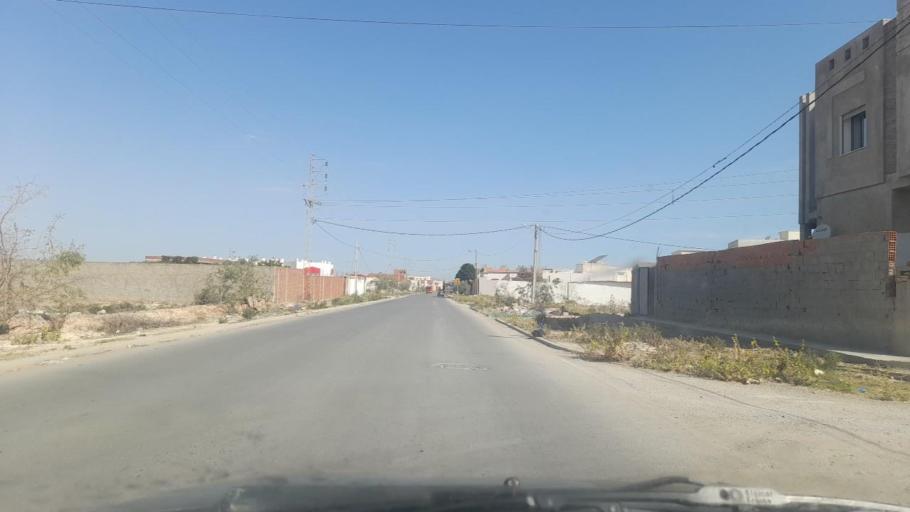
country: TN
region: Susah
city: Akouda
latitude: 35.8143
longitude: 10.5581
